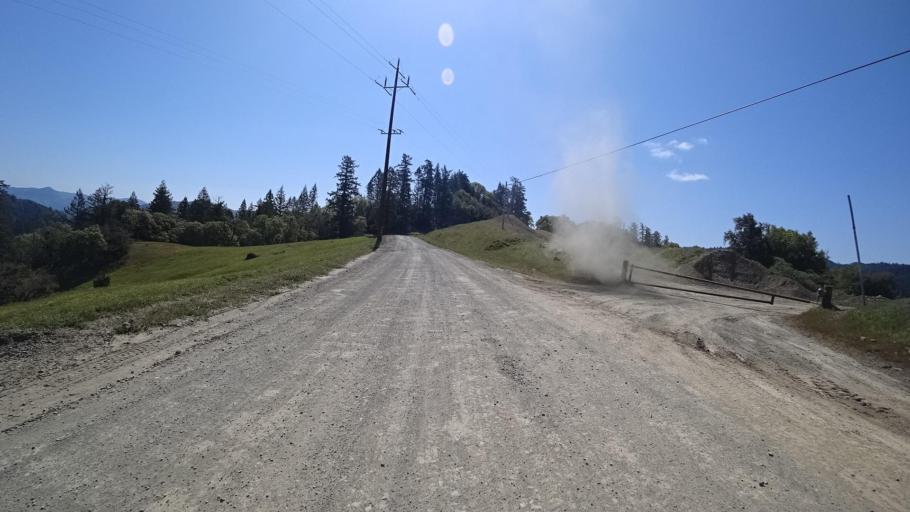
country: US
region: California
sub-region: Humboldt County
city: Redway
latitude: 40.0222
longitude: -123.6277
